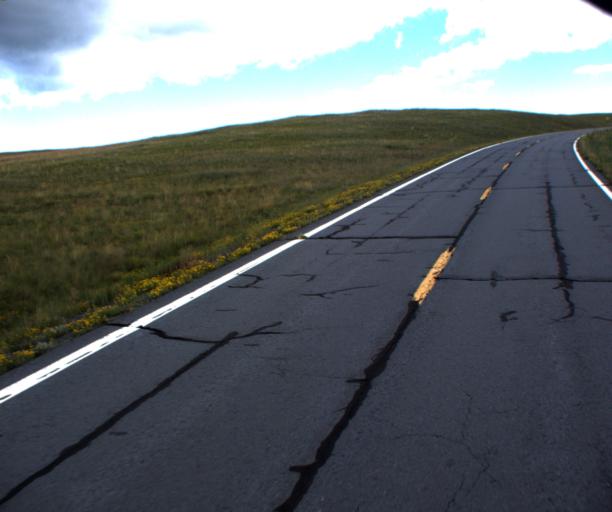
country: US
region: Arizona
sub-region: Apache County
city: Eagar
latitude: 33.9537
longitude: -109.3965
